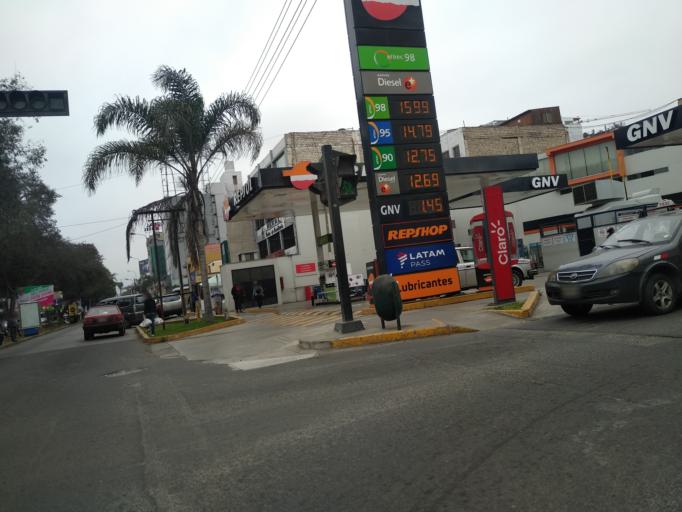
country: PE
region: Lima
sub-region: Lima
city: San Isidro
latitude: -12.1023
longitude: -77.0212
